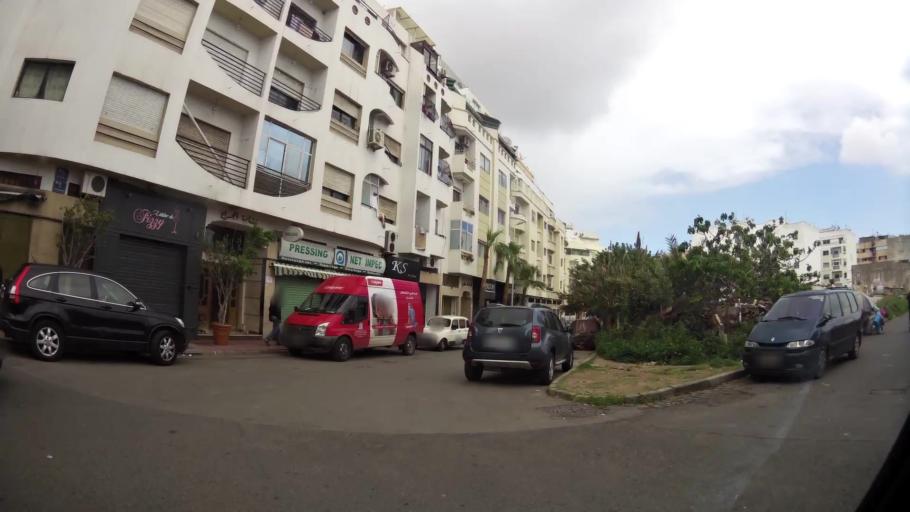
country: MA
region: Grand Casablanca
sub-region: Casablanca
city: Casablanca
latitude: 33.5962
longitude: -7.6451
